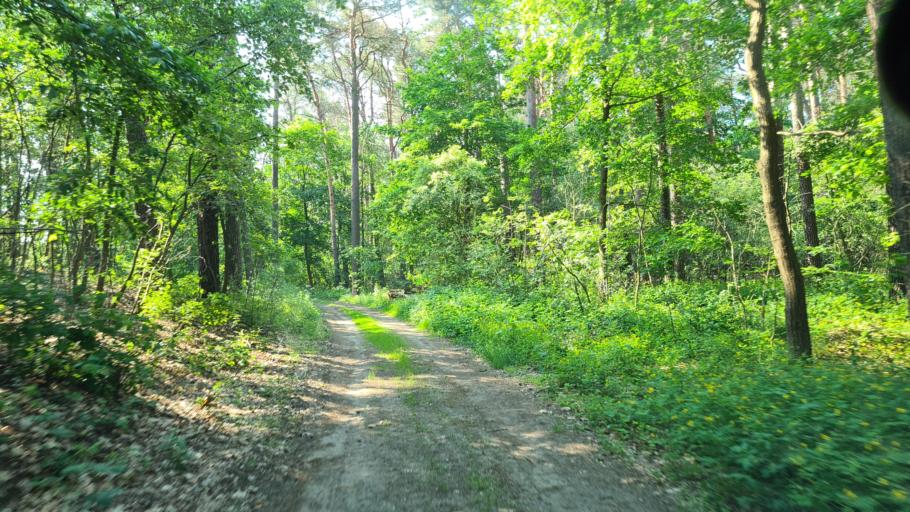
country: DE
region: Brandenburg
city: Hohenbucko
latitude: 51.6962
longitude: 13.5080
